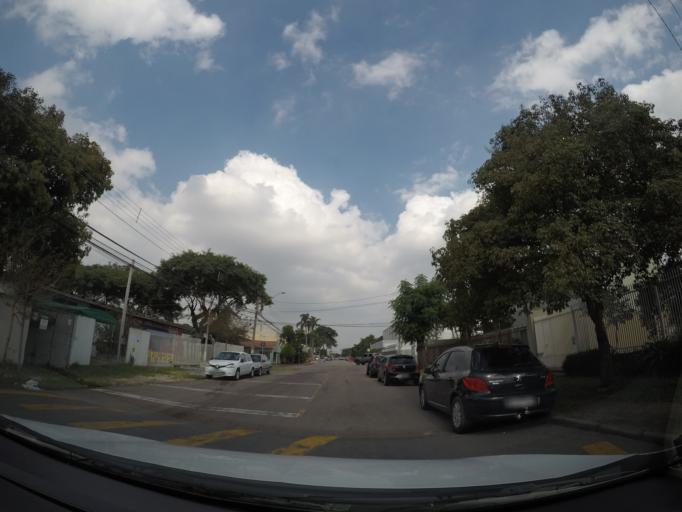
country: BR
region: Parana
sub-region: Curitiba
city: Curitiba
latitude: -25.4768
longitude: -49.2550
